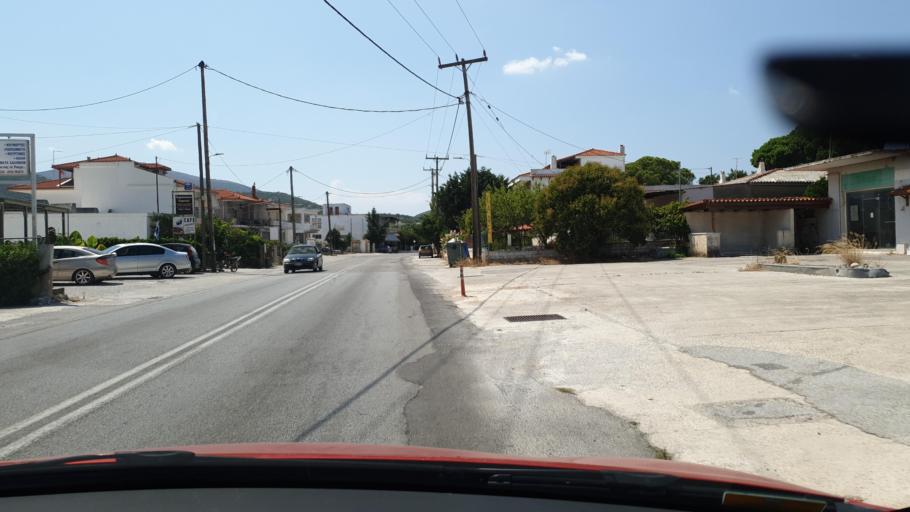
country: GR
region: Central Greece
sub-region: Nomos Evvoias
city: Aliveri
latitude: 38.3933
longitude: 24.0967
